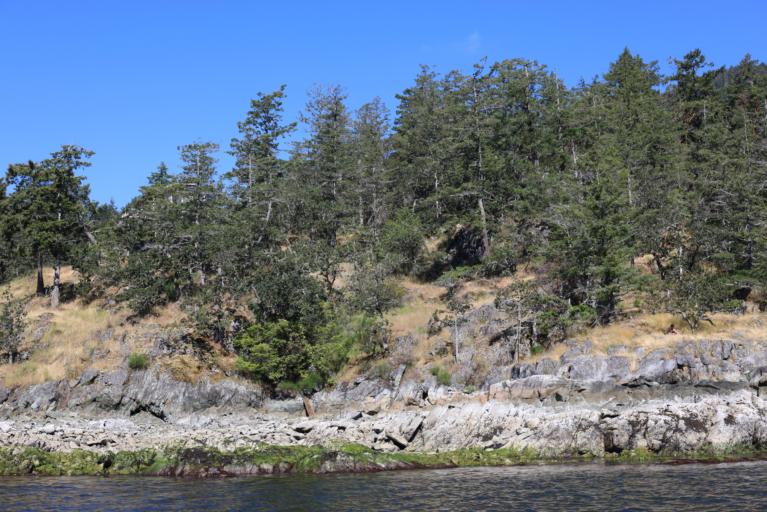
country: CA
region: British Columbia
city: North Cowichan
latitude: 48.8221
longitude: -123.5852
